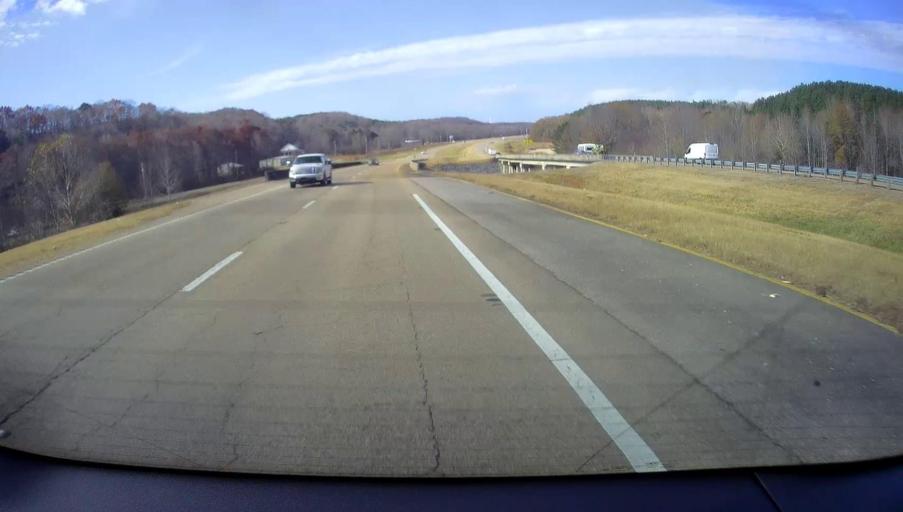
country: US
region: Mississippi
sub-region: Alcorn County
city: Corinth
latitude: 34.9326
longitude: -88.7669
